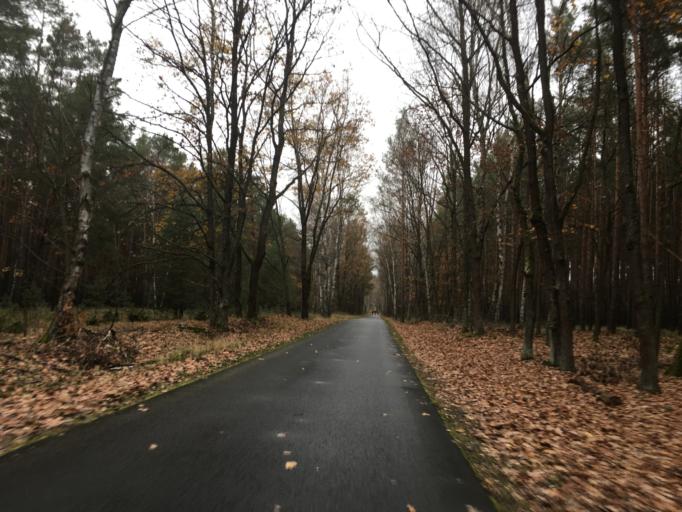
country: DE
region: Brandenburg
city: Mullrose
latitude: 52.2384
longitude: 14.4498
